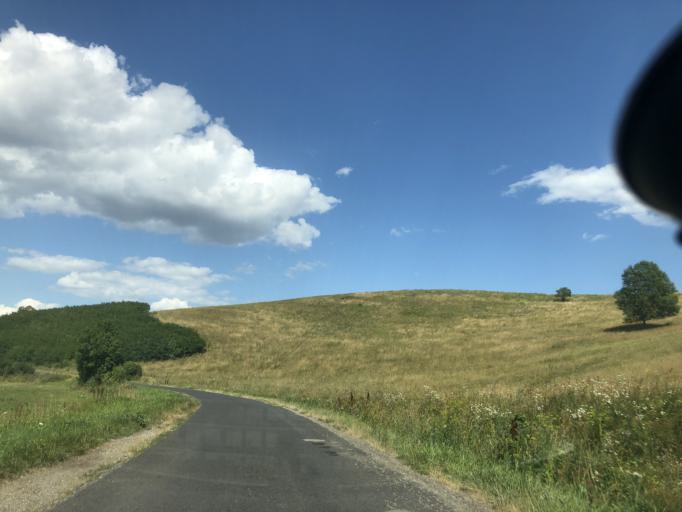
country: HU
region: Borsod-Abauj-Zemplen
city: Szendro
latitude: 48.5432
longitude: 20.7974
